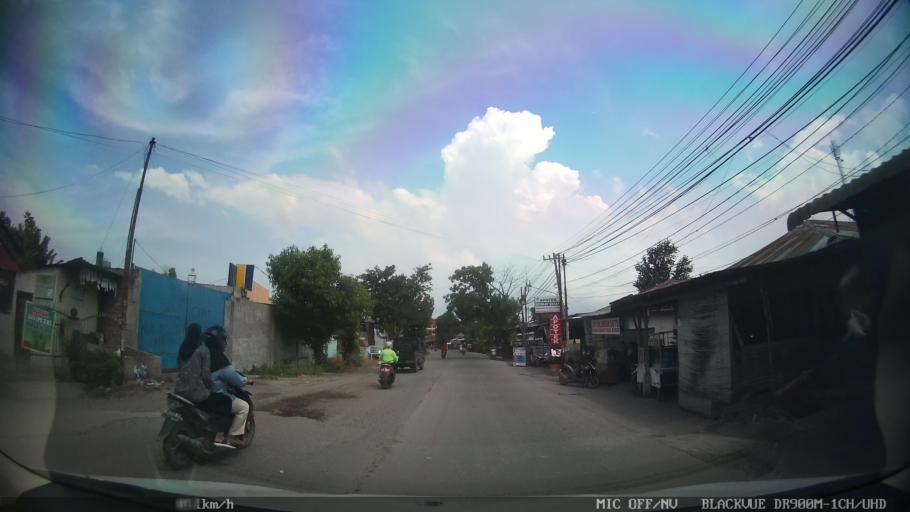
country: ID
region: North Sumatra
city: Labuhan Deli
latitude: 3.6701
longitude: 98.6786
